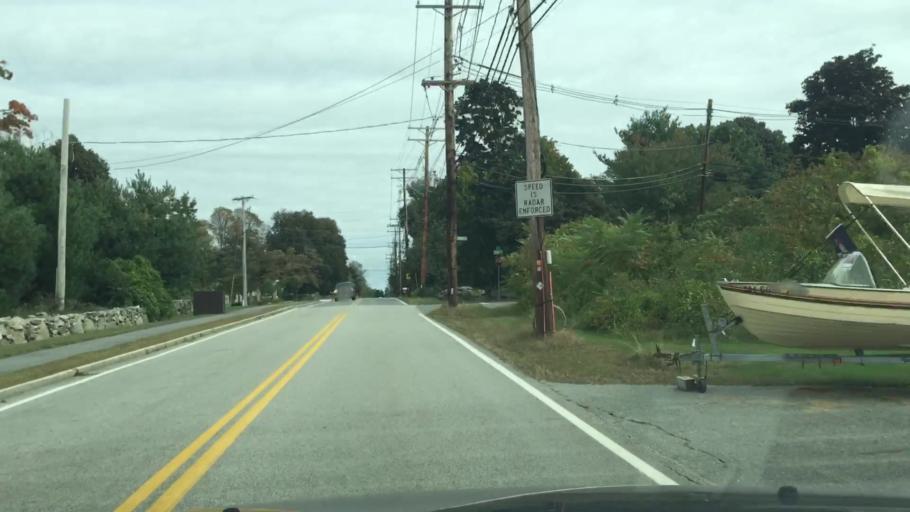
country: US
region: Massachusetts
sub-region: Middlesex County
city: Tewksbury
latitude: 42.6538
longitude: -71.2477
